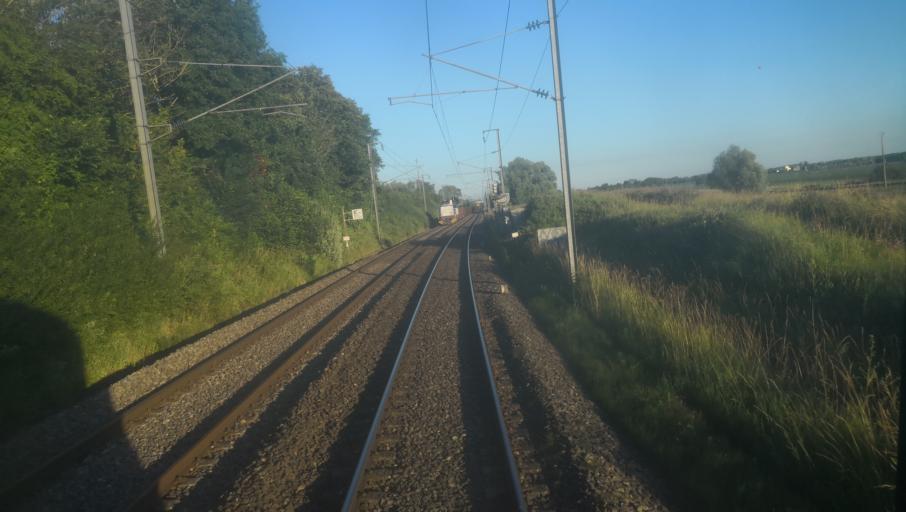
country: FR
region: Auvergne
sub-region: Departement de l'Allier
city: Trevol
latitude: 46.6530
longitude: 3.2631
